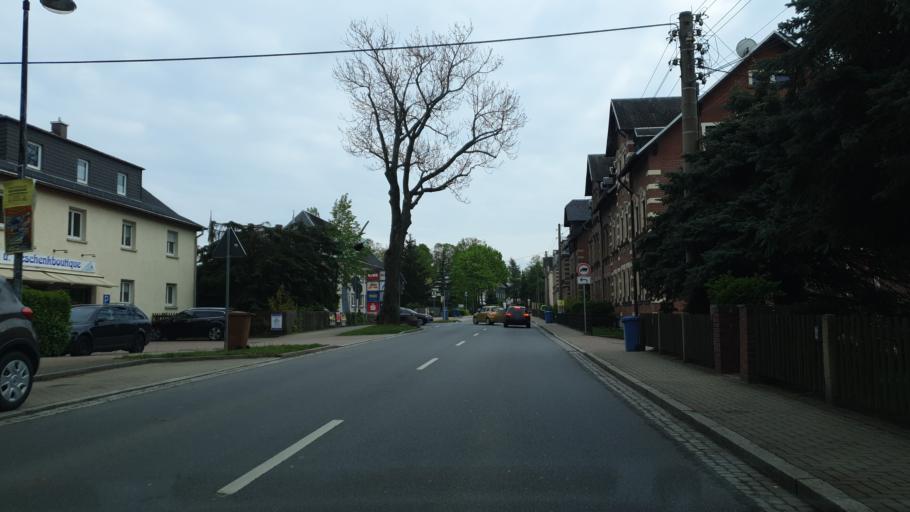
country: DE
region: Saxony
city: Lugau
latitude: 50.7452
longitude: 12.7460
